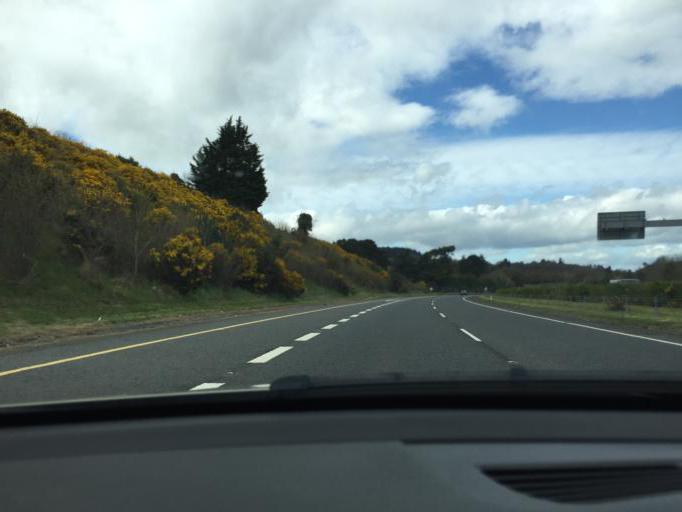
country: IE
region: Leinster
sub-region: Wicklow
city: Ashford
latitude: 53.0476
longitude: -6.0913
